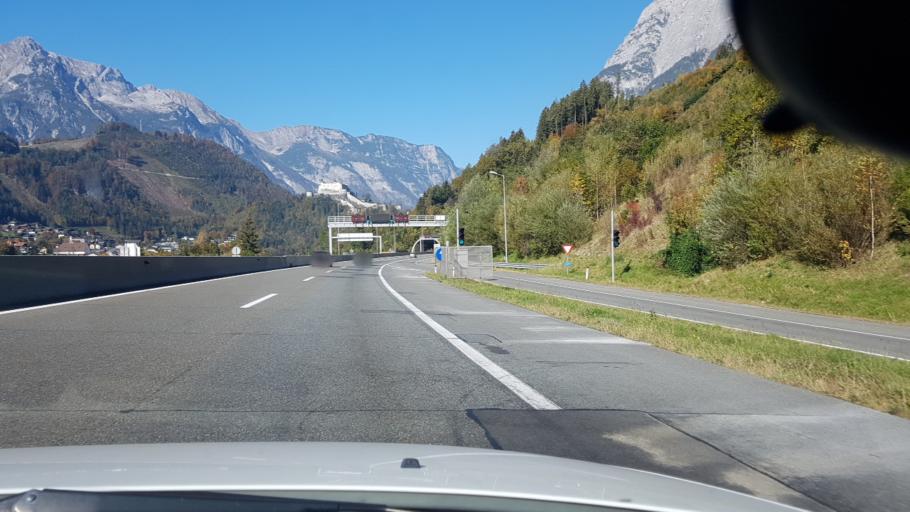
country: AT
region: Salzburg
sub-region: Politischer Bezirk Sankt Johann im Pongau
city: Pfarrwerfen
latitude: 47.4697
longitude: 13.1999
